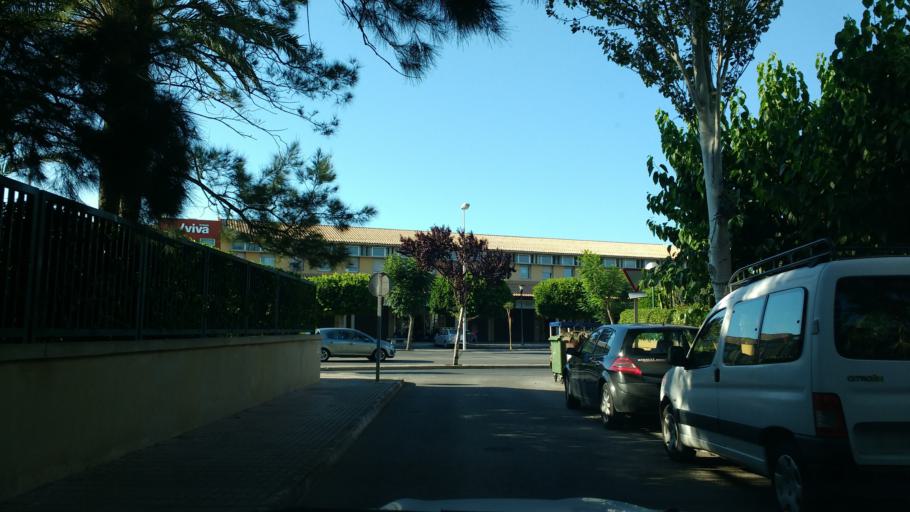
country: ES
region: Balearic Islands
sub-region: Illes Balears
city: Port d'Alcudia
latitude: 39.8402
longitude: 3.1246
